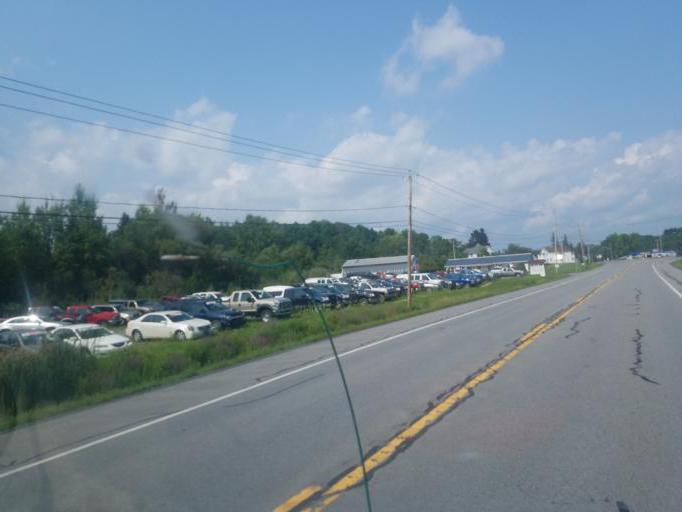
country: US
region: New York
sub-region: Fulton County
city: Johnstown
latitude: 42.9904
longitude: -74.3833
